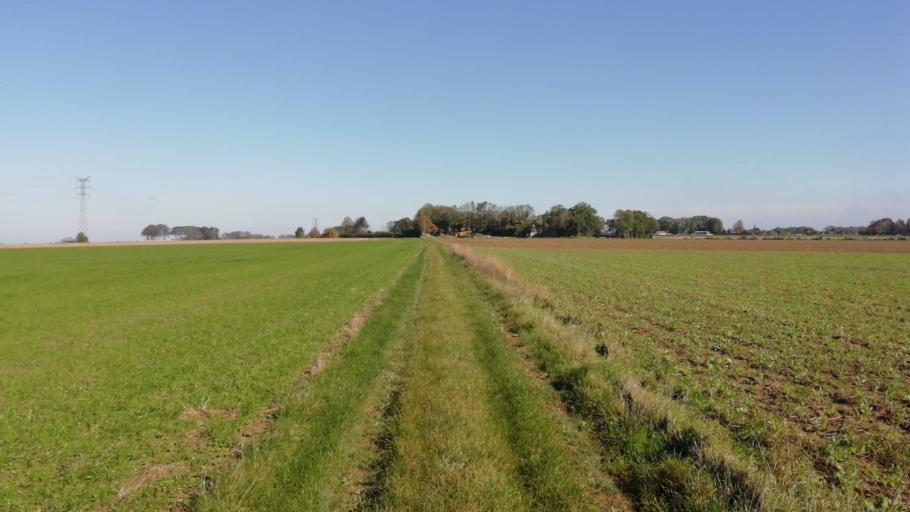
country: FR
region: Haute-Normandie
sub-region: Departement de la Seine-Maritime
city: Maneglise
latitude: 49.5817
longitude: 0.2648
